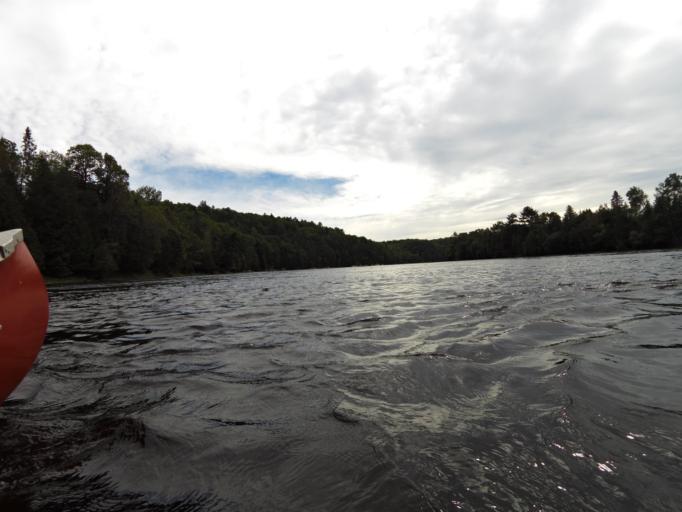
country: CA
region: Quebec
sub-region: Outaouais
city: Wakefield
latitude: 45.7641
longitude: -75.9253
